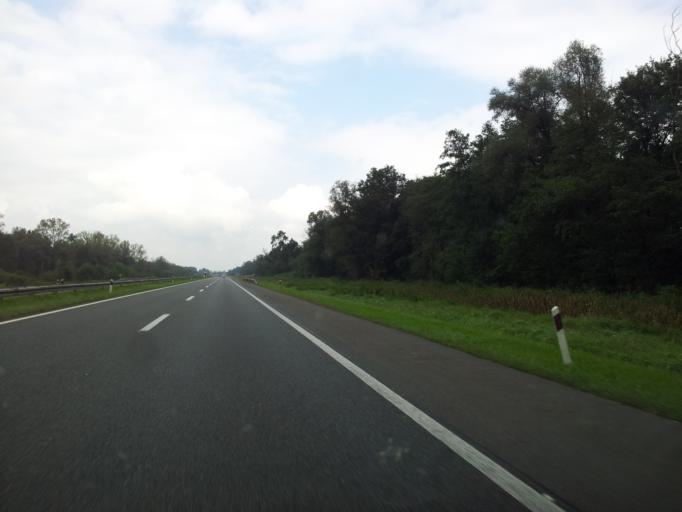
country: HR
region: Sisacko-Moslavacka
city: Lipovljani
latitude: 45.4226
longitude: 16.8427
